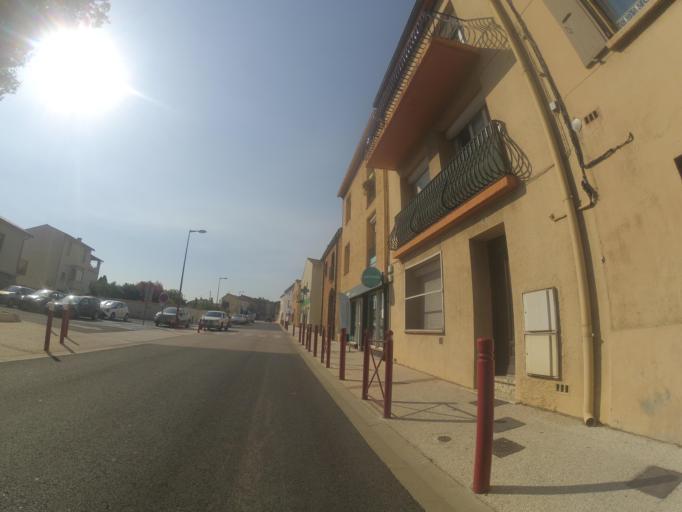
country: FR
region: Languedoc-Roussillon
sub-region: Departement des Pyrenees-Orientales
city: Toulouges
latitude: 42.6698
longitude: 2.8309
